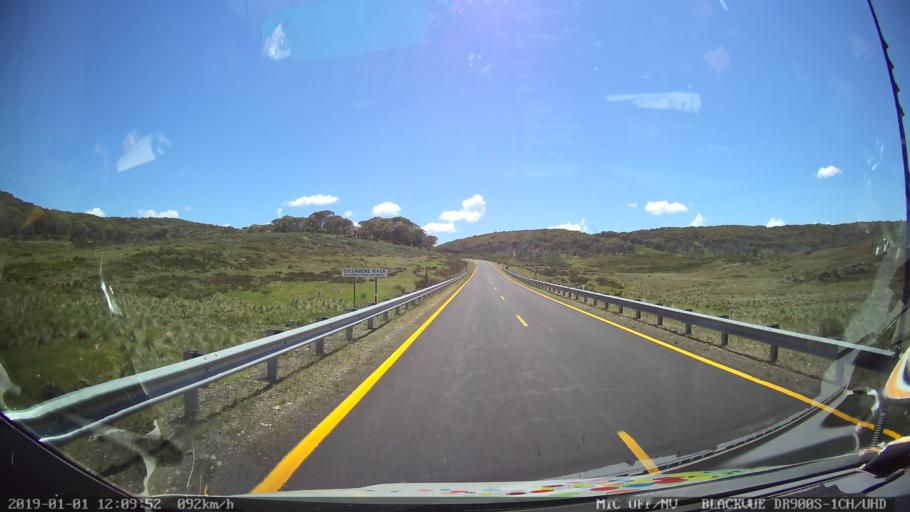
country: AU
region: New South Wales
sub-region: Tumut Shire
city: Tumut
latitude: -35.8025
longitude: 148.4972
